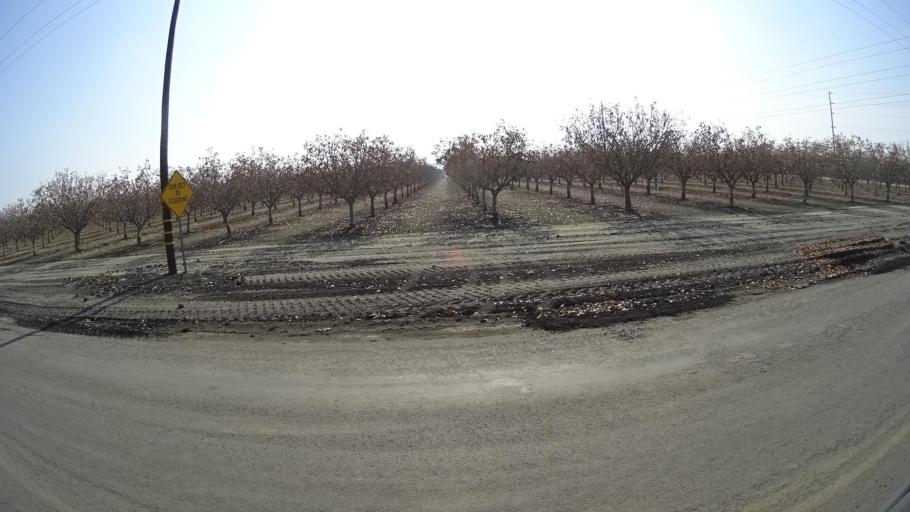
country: US
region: California
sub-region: Kern County
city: Buttonwillow
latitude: 35.3693
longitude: -119.4466
